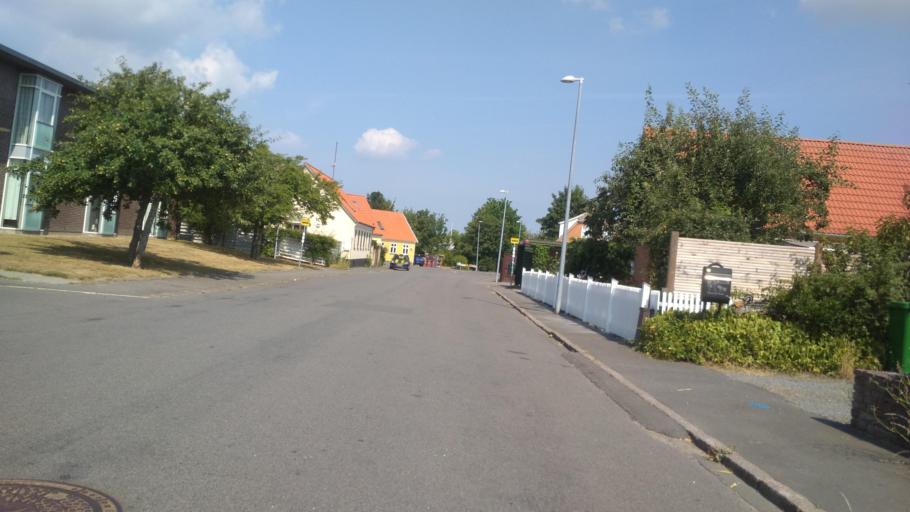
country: DK
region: Capital Region
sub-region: Bornholm Kommune
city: Akirkeby
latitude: 55.0701
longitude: 14.9273
